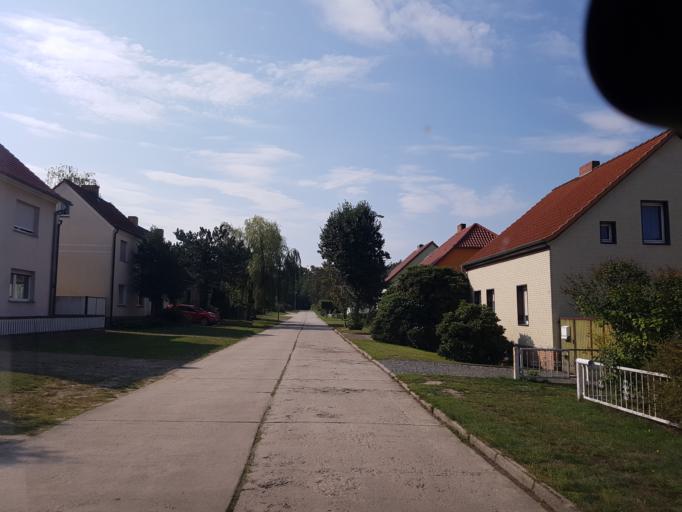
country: DE
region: Brandenburg
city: Plessa
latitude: 51.5317
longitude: 13.6658
